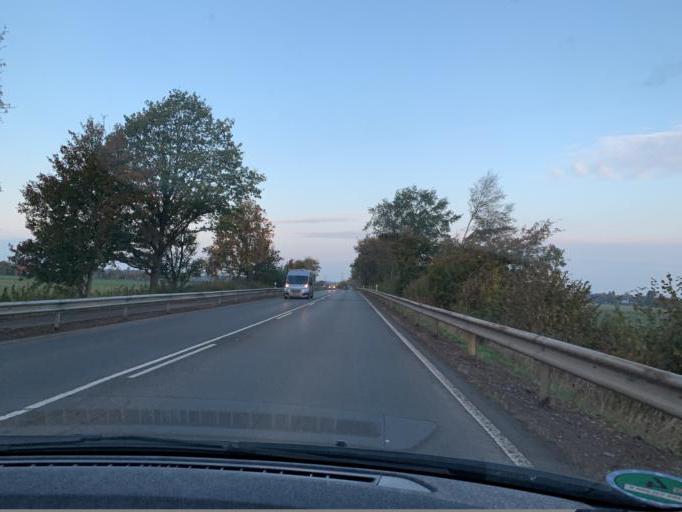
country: DE
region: North Rhine-Westphalia
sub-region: Regierungsbezirk Dusseldorf
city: Juchen
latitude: 51.1143
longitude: 6.4729
